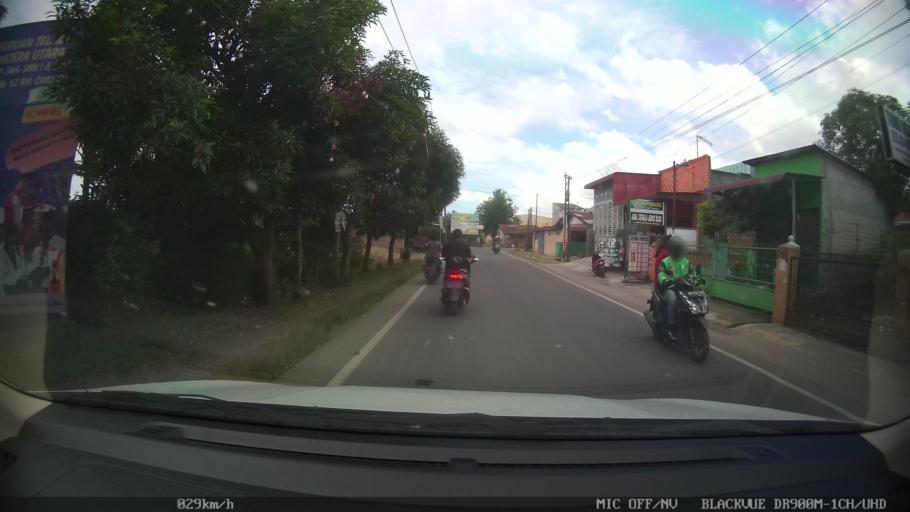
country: ID
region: North Sumatra
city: Sunggal
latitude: 3.6178
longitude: 98.6235
